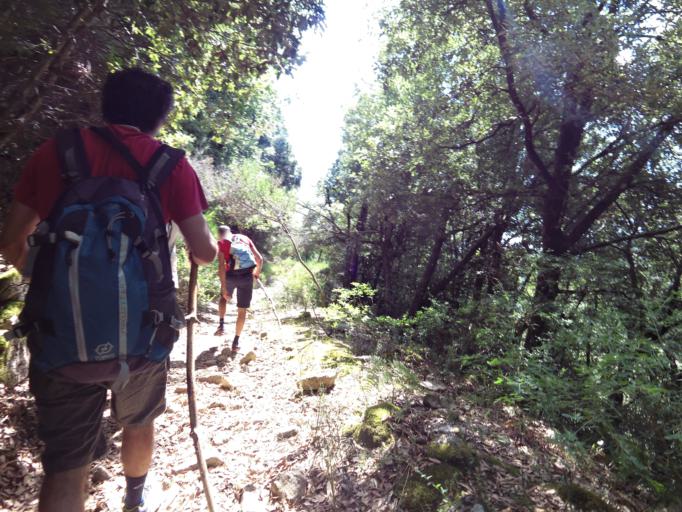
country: IT
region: Calabria
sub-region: Provincia di Vibo-Valentia
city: Nardodipace
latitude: 38.5074
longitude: 16.3875
